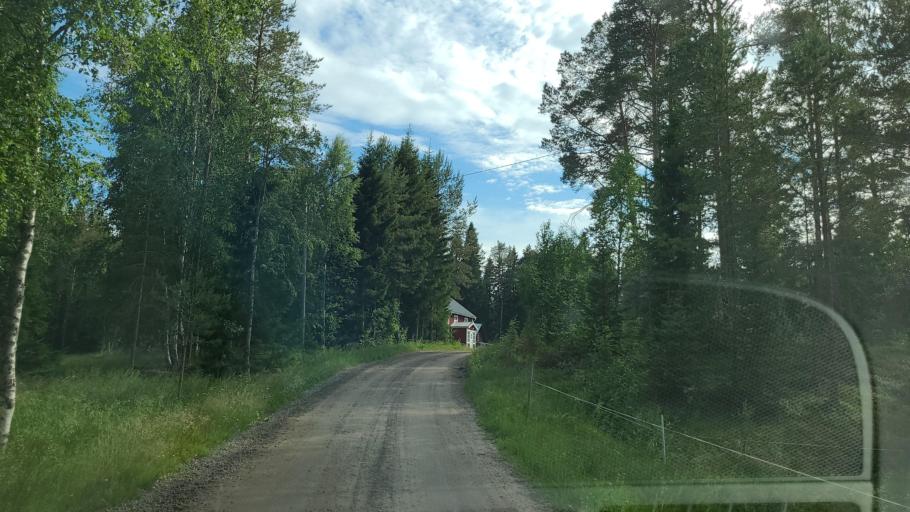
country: SE
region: Vaesterbotten
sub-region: Robertsfors Kommun
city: Robertsfors
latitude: 64.1552
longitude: 20.9240
